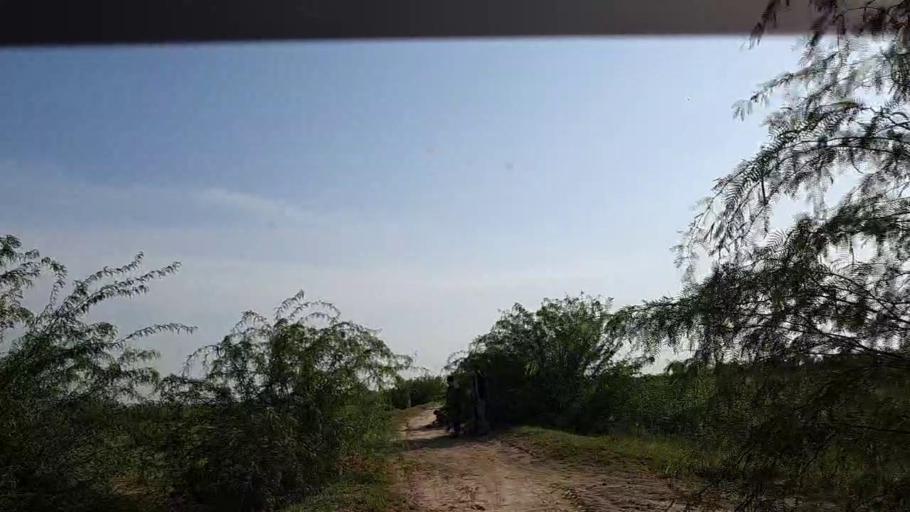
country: PK
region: Sindh
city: Adilpur
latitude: 27.9027
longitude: 69.2322
